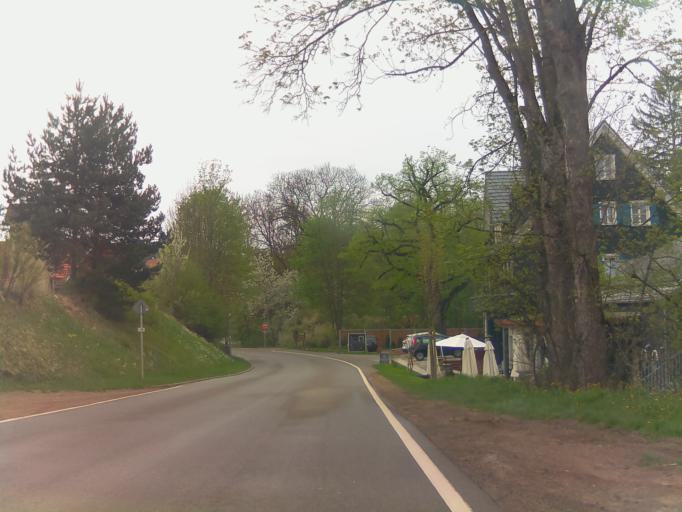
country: DE
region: Baden-Wuerttemberg
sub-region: Freiburg Region
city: Niedereschach
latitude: 48.1128
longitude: 8.5086
